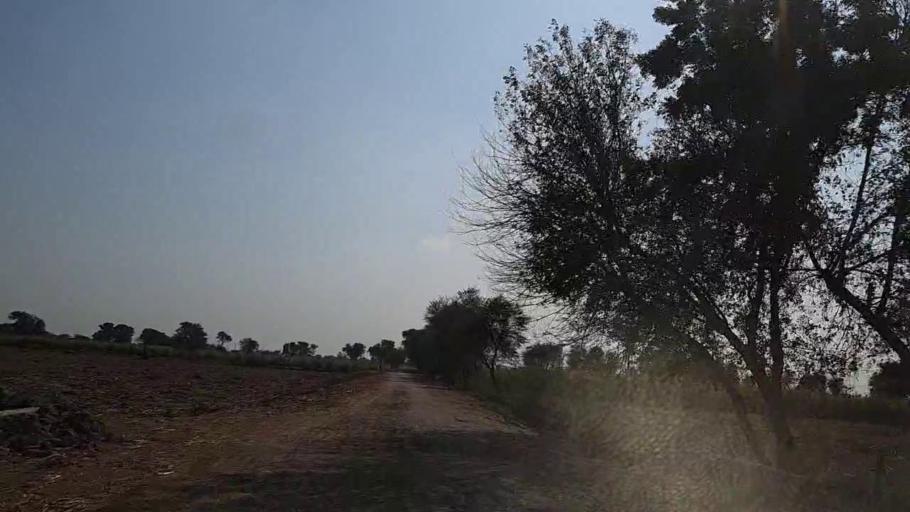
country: PK
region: Sindh
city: Daur
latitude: 26.4374
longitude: 68.2333
